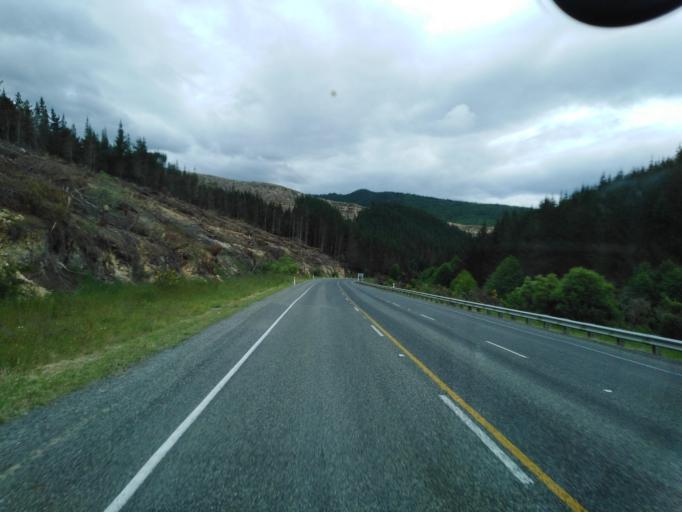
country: NZ
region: Tasman
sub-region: Tasman District
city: Wakefield
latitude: -41.4867
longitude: 172.9003
